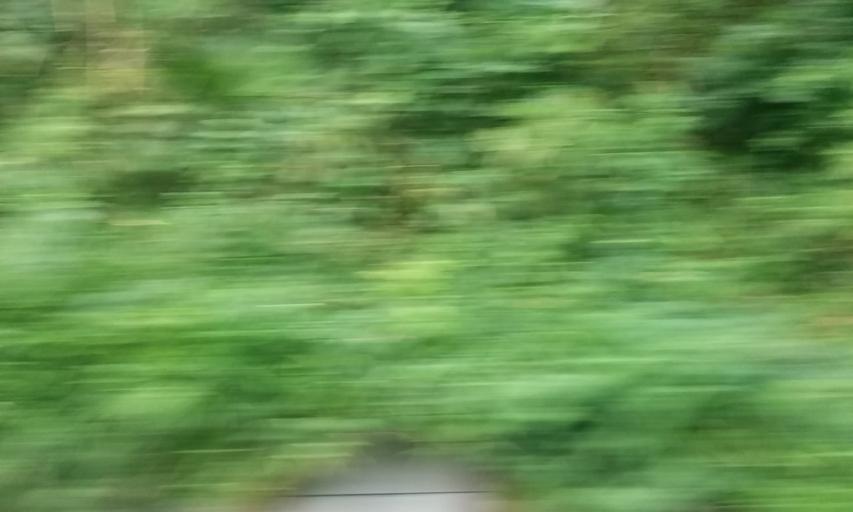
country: JP
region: Chiba
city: Nagareyama
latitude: 35.8316
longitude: 139.9198
